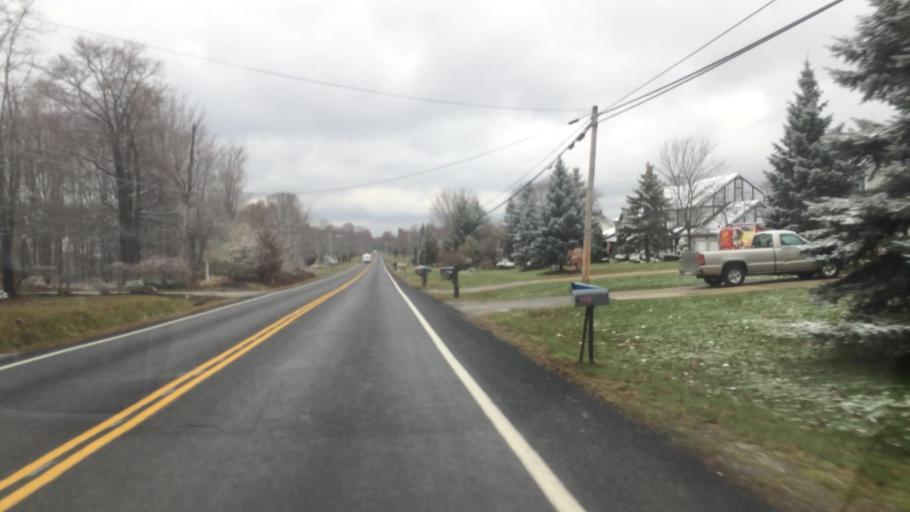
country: US
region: Ohio
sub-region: Summit County
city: Boston Heights
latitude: 41.2812
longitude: -81.5153
